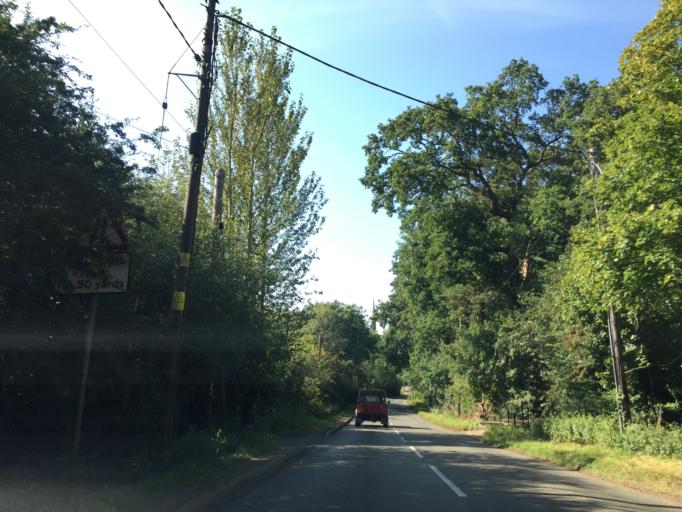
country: GB
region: England
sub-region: Leicestershire
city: Queniborough
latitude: 52.7017
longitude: -1.0338
